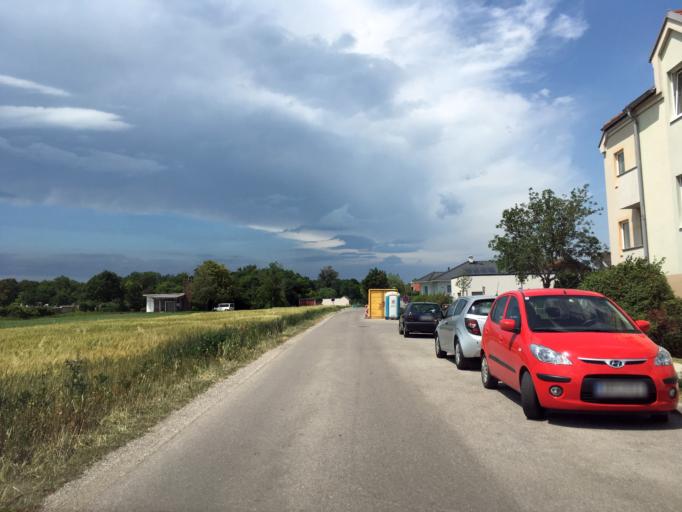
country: AT
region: Lower Austria
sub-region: Politischer Bezirk Baden
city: Teesdorf
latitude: 47.9473
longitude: 16.2779
